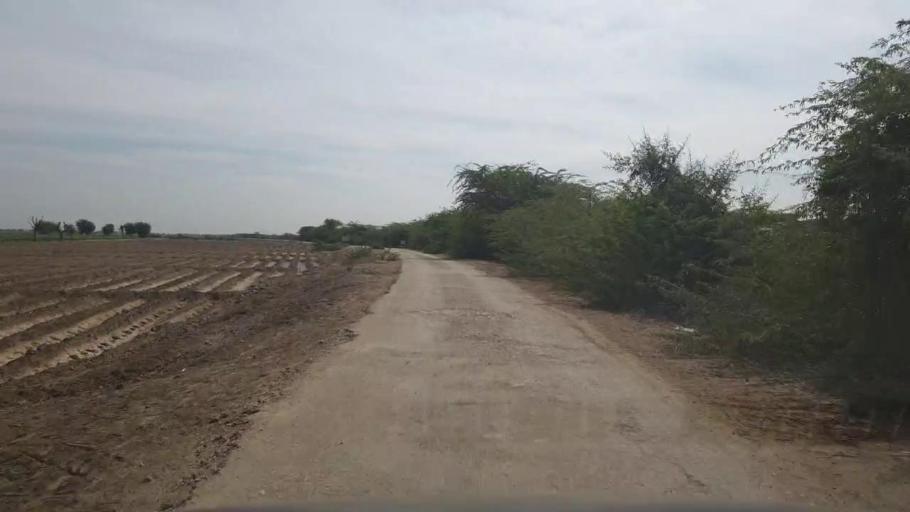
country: PK
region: Sindh
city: Kunri
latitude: 25.2744
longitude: 69.5979
